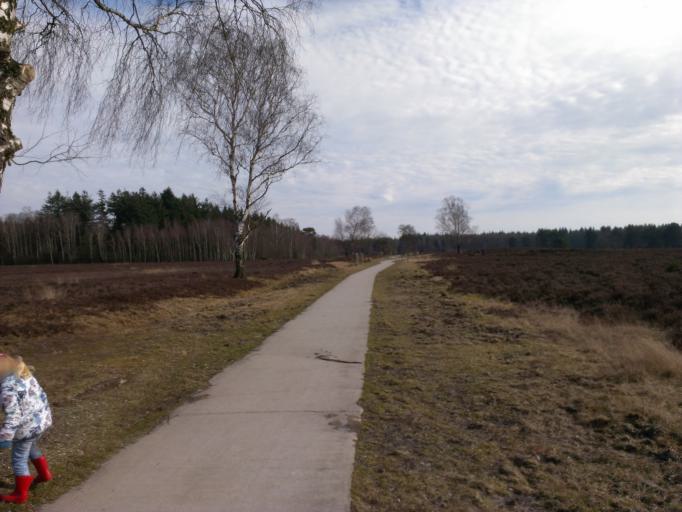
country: NL
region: Gelderland
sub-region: Gemeente Epe
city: Epe
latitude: 52.3890
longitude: 5.9854
